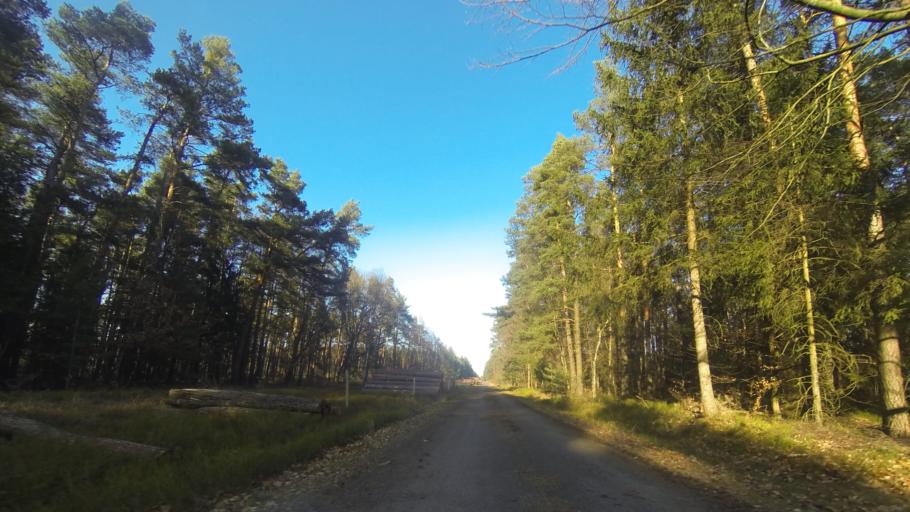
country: DE
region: Saxony
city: Tauscha
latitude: 51.2410
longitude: 13.8174
